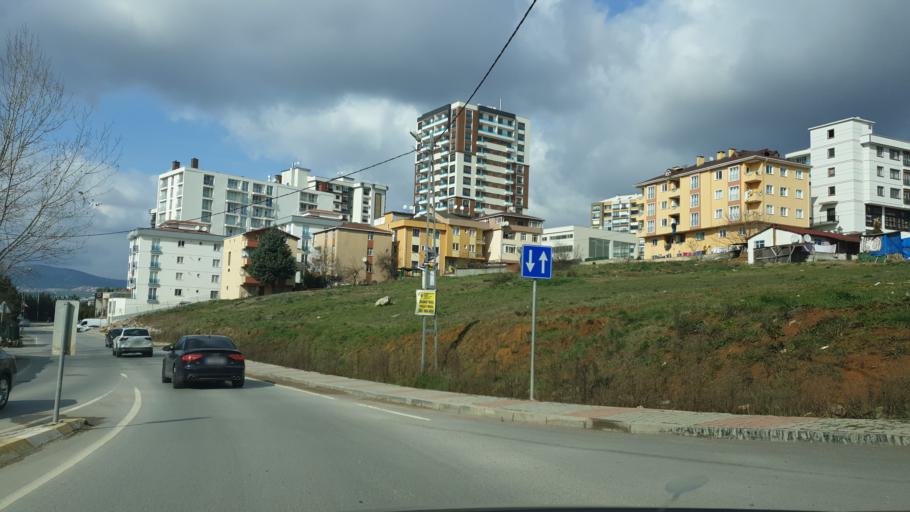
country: TR
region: Istanbul
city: Icmeler
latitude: 40.8723
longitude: 29.3241
